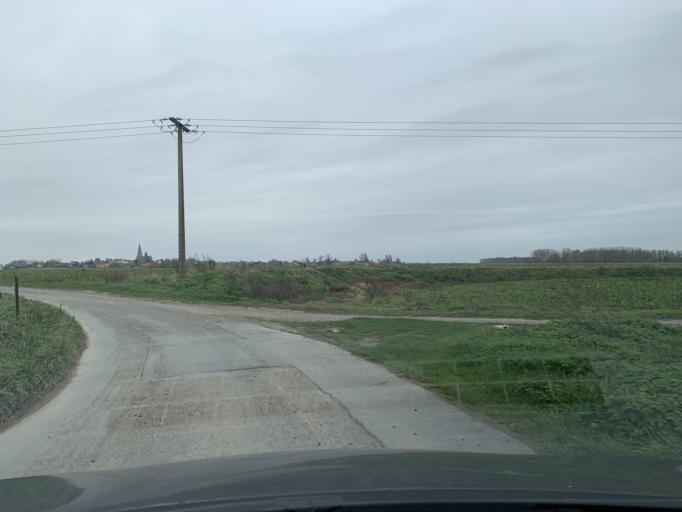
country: FR
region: Nord-Pas-de-Calais
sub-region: Departement du Pas-de-Calais
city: Oisy-le-Verger
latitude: 50.2485
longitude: 3.1010
